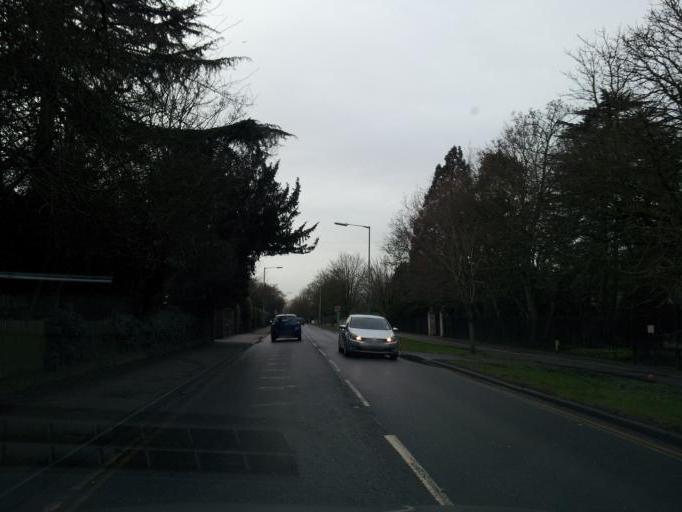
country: GB
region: England
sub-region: Cambridgeshire
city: Cambridge
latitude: 52.1975
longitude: 0.1007
